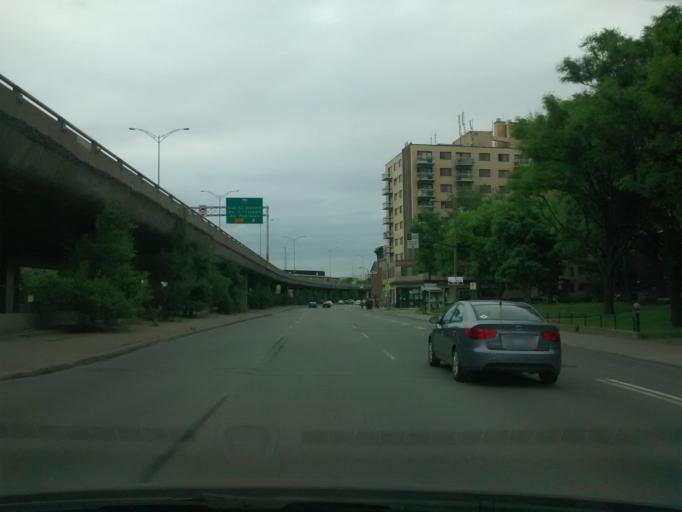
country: CA
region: Quebec
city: Mont-Royal
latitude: 45.5466
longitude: -73.6376
